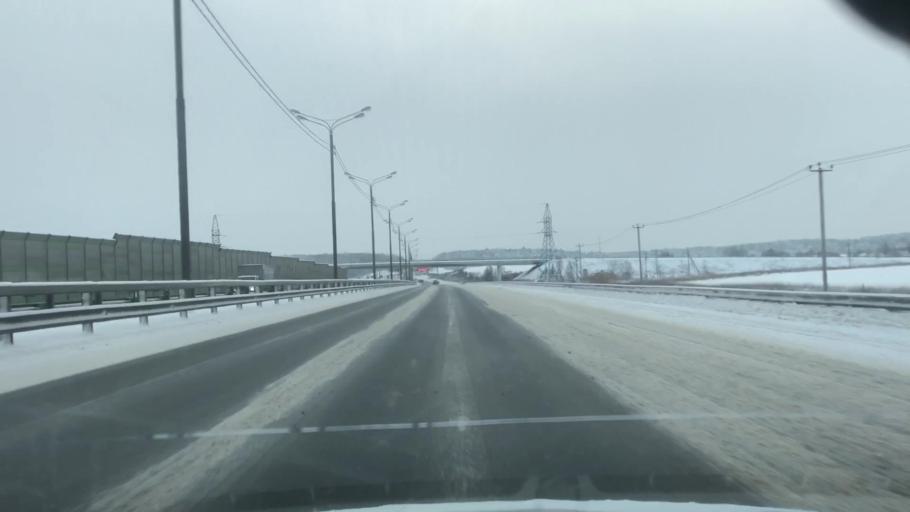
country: RU
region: Moskovskaya
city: Mikhnevo
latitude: 55.1893
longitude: 37.8968
